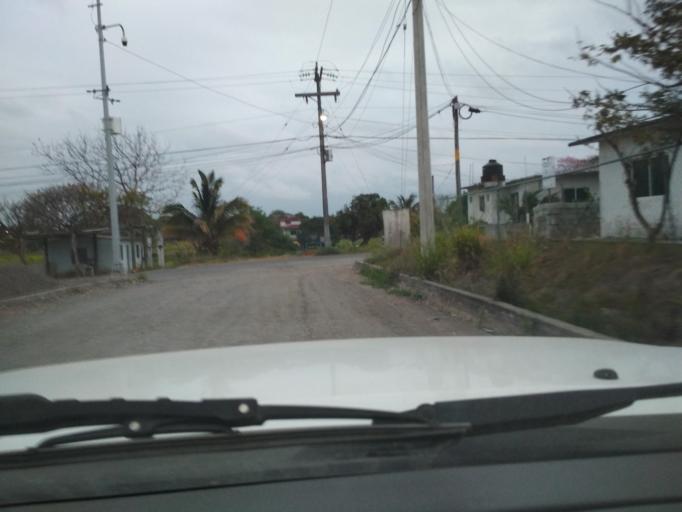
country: MX
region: Veracruz
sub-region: Medellin
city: Fraccionamiento Arboledas San Ramon
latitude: 19.0898
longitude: -96.1294
